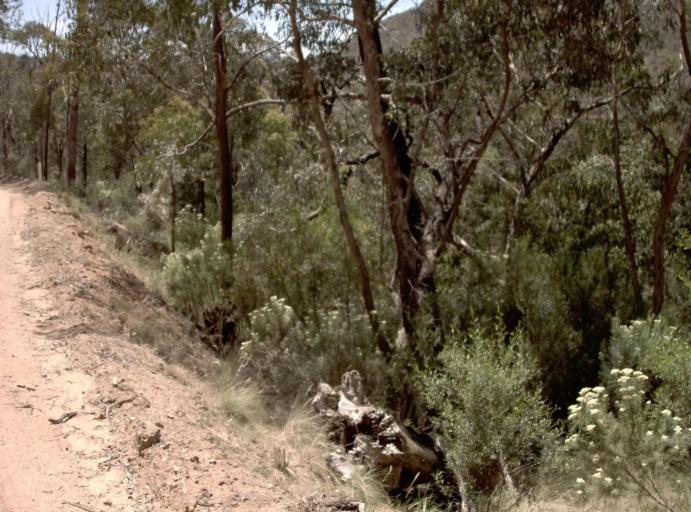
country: AU
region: New South Wales
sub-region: Snowy River
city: Jindabyne
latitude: -36.9748
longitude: 148.3014
